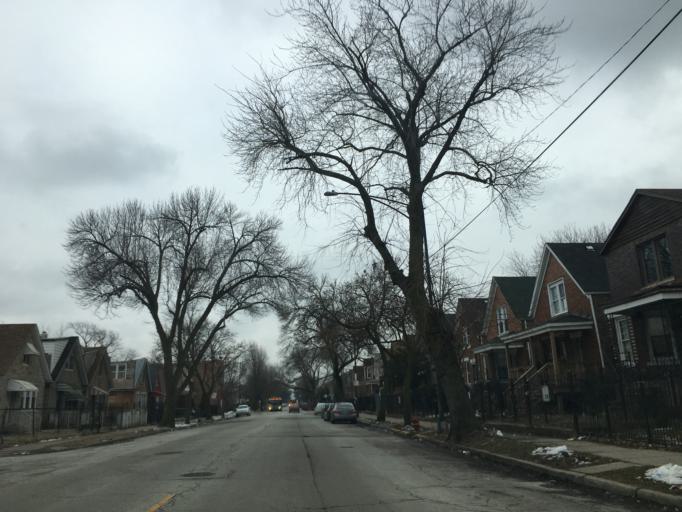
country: US
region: Illinois
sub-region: Cook County
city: Cicero
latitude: 41.8984
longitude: -87.7115
